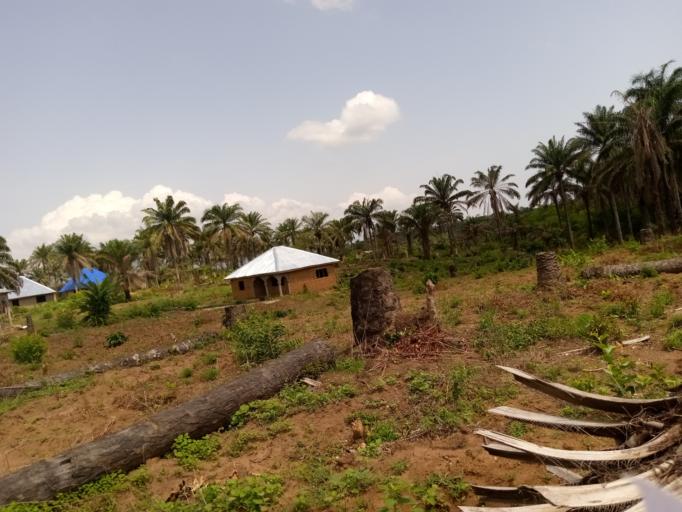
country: SL
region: Western Area
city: Waterloo
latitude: 8.3562
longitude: -13.0110
